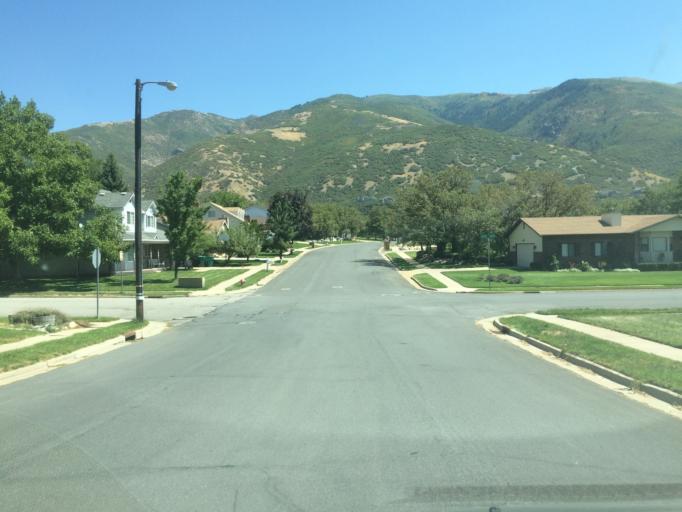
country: US
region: Utah
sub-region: Davis County
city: South Weber
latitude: 41.1130
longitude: -111.9171
